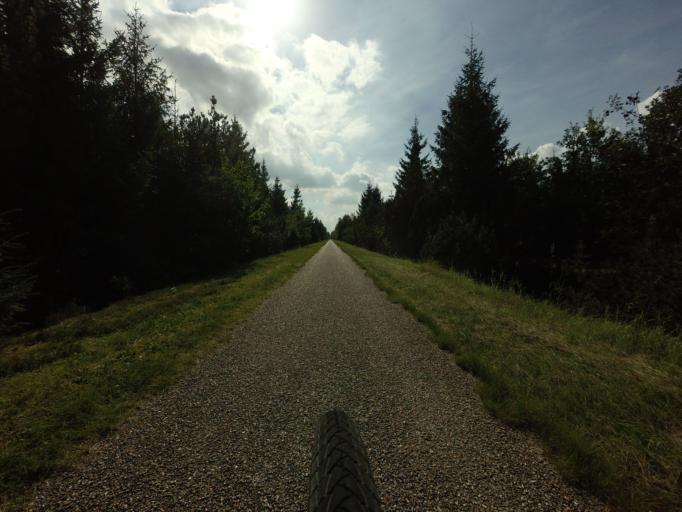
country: DK
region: Central Jutland
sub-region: Viborg Kommune
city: Karup
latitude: 56.2499
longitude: 9.1021
